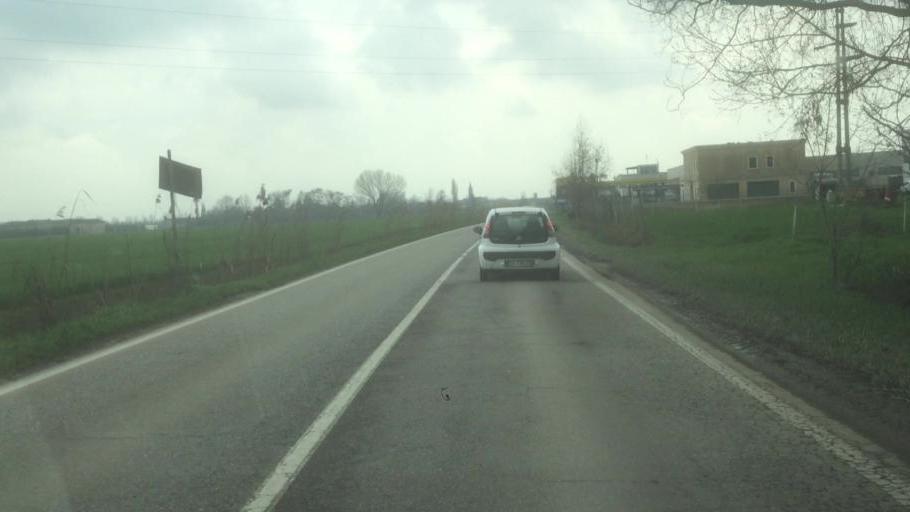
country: IT
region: Lombardy
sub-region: Provincia di Mantova
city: Casaloldo
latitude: 45.2663
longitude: 10.4773
